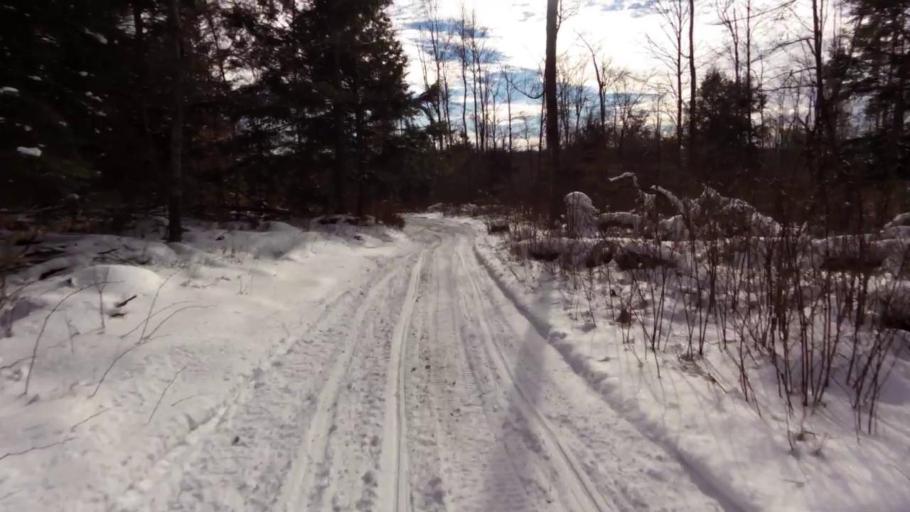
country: US
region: Pennsylvania
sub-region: McKean County
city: Foster Brook
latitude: 42.0063
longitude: -78.5422
